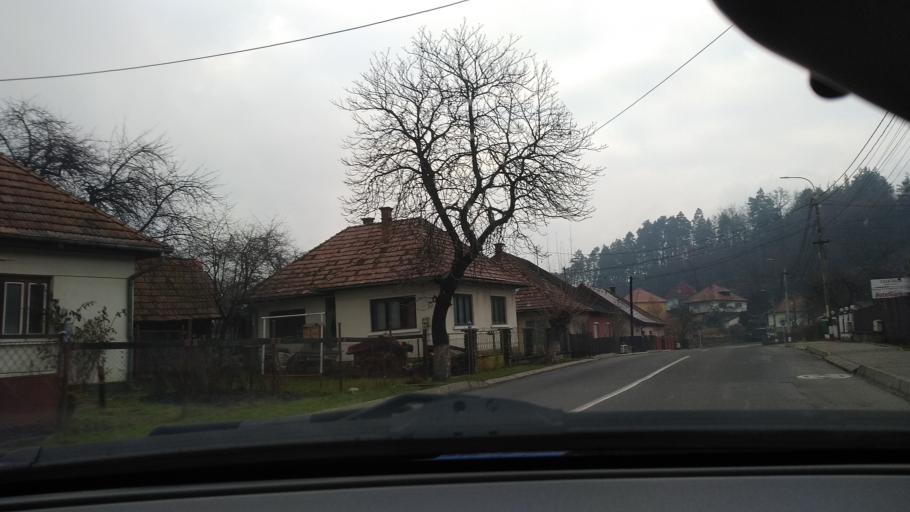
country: RO
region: Mures
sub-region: Oras Sovata
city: Sovata
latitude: 46.5971
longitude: 25.0745
